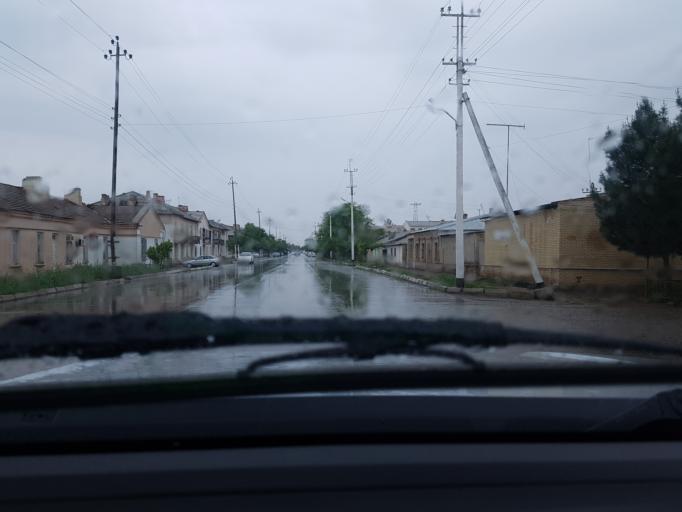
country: TM
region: Lebap
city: Turkmenabat
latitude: 39.1032
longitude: 63.5780
